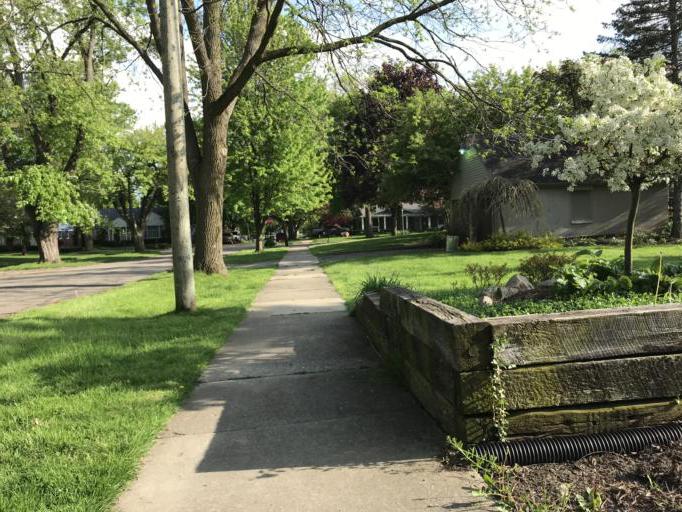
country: US
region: Michigan
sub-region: Oakland County
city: Farmington
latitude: 42.4645
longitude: -83.3800
